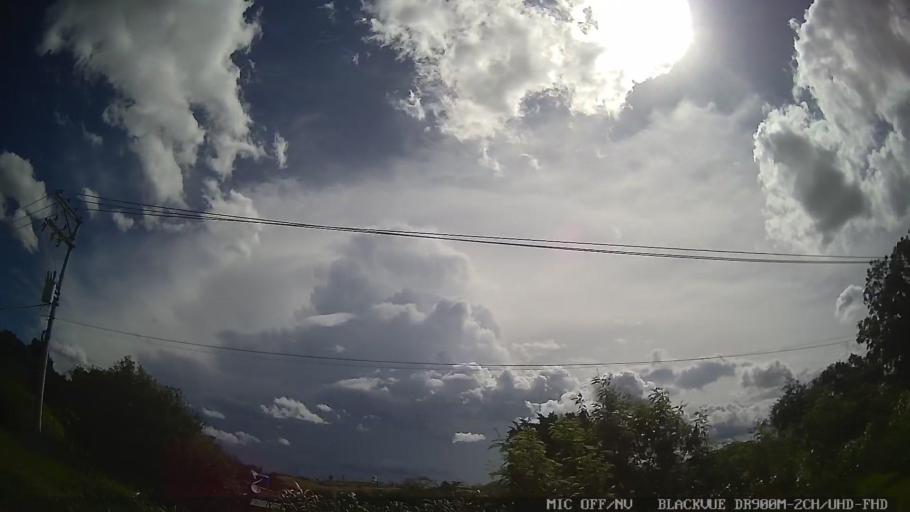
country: BR
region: Sao Paulo
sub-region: Amparo
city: Amparo
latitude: -22.7135
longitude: -46.8169
